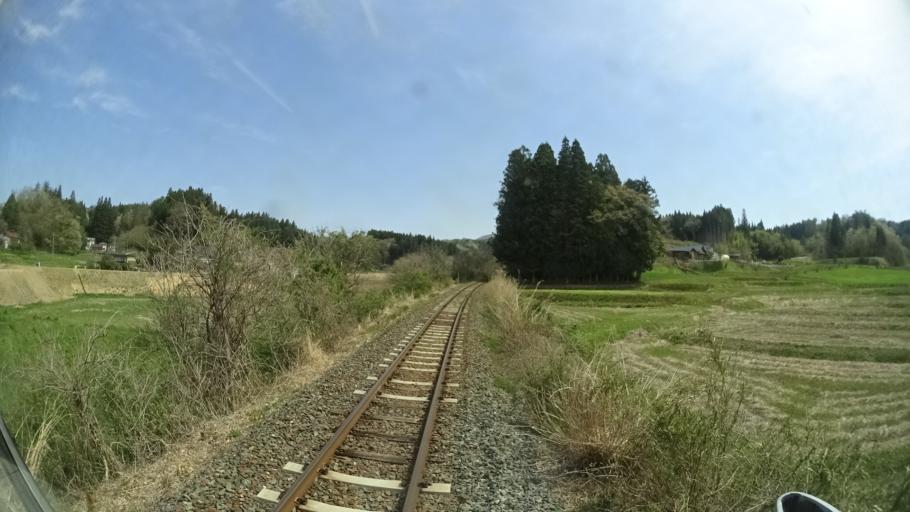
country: JP
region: Iwate
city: Ichinoseki
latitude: 38.9348
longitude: 141.3880
